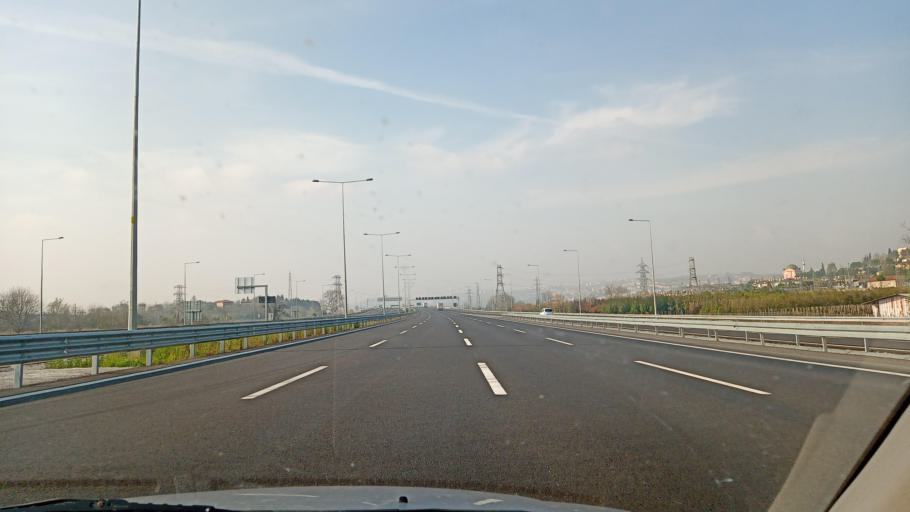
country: TR
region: Sakarya
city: Kazimpasa
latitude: 40.8433
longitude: 30.3414
